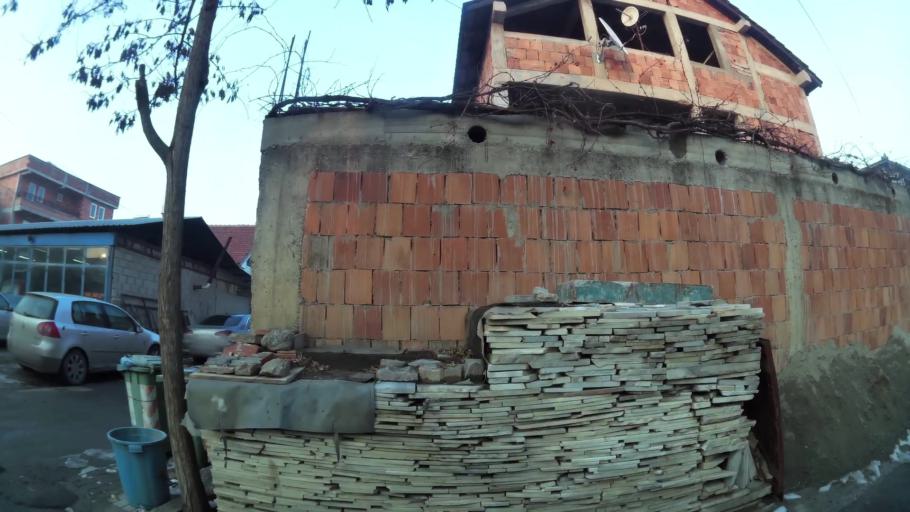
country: MK
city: Creshevo
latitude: 42.0145
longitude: 21.5118
